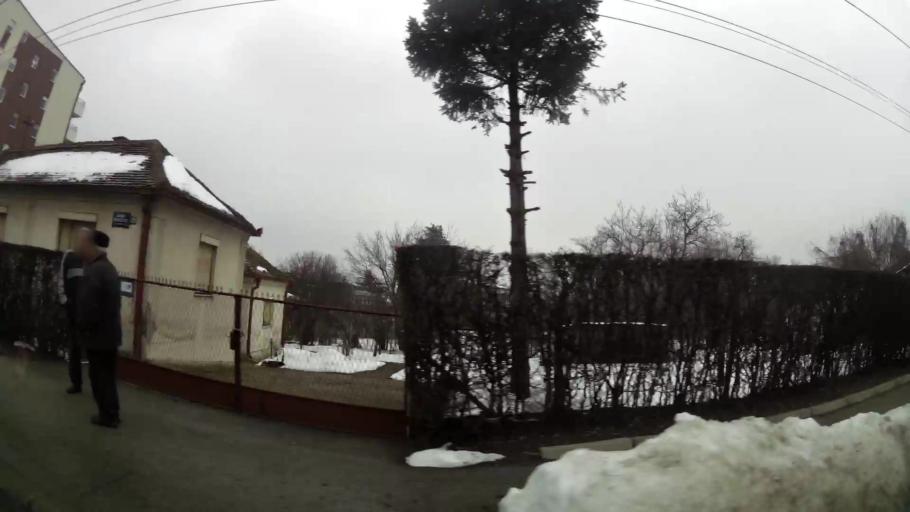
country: RS
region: Central Serbia
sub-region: Belgrade
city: Vozdovac
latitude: 44.7506
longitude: 20.4938
